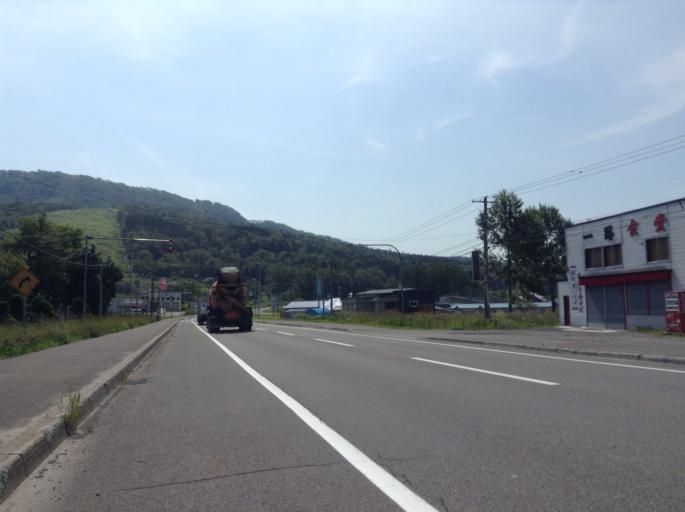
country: JP
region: Hokkaido
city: Nayoro
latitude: 44.7240
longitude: 142.2667
